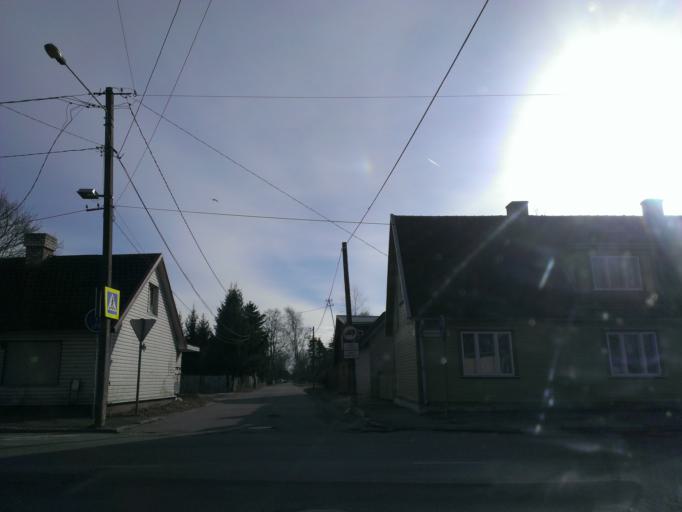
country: EE
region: Paernumaa
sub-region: Paernu linn
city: Parnu
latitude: 58.3901
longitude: 24.4693
